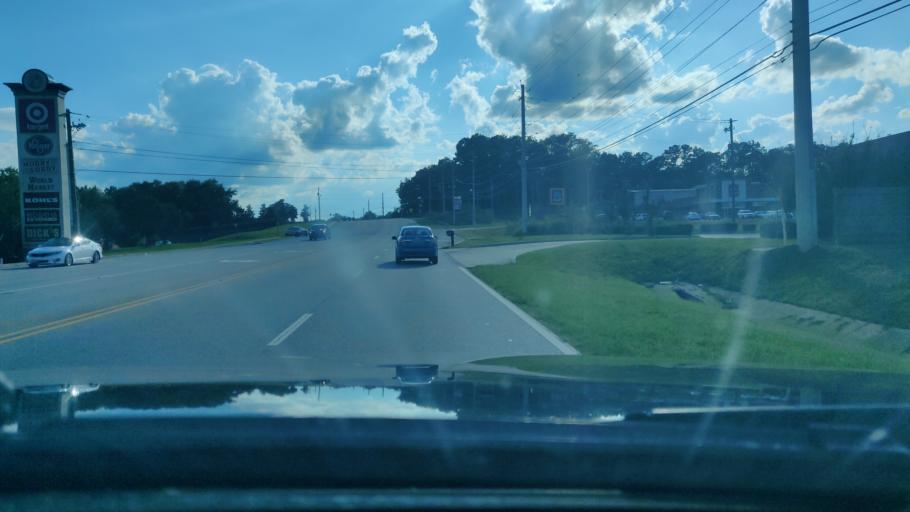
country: US
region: Alabama
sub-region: Lee County
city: Opelika
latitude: 32.6222
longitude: -85.4101
